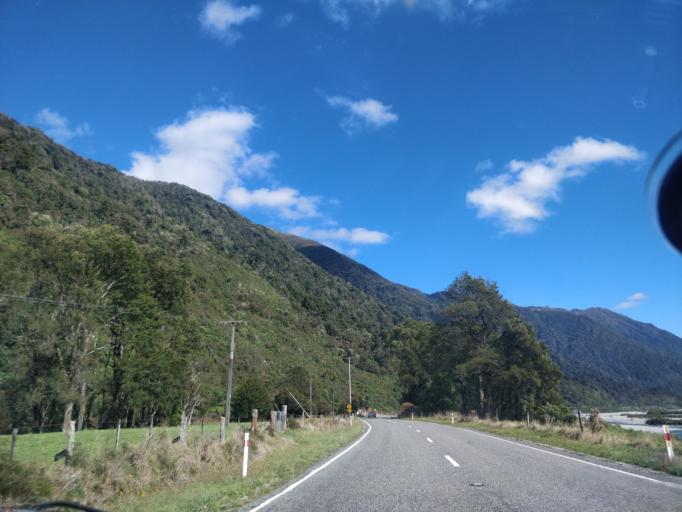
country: NZ
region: West Coast
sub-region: Grey District
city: Greymouth
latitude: -42.7624
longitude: 171.6069
